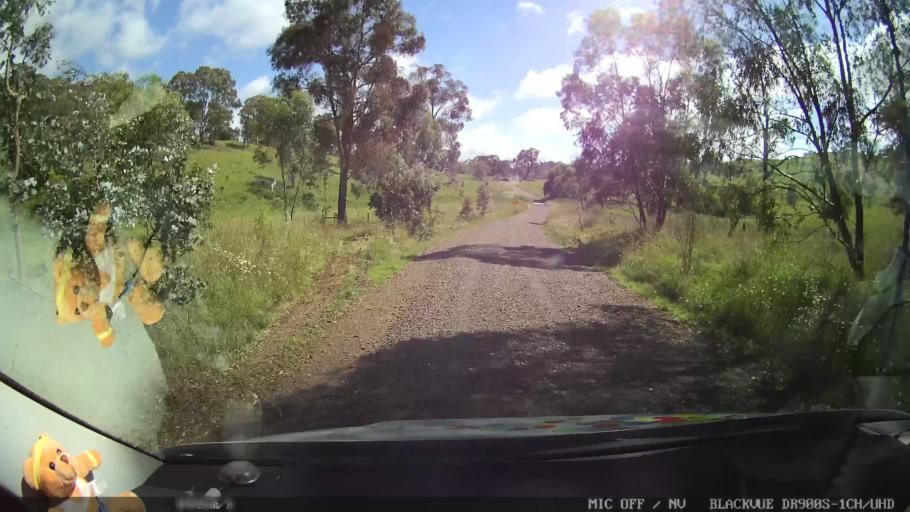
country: AU
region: New South Wales
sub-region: Guyra
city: Guyra
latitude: -29.9837
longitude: 151.6949
